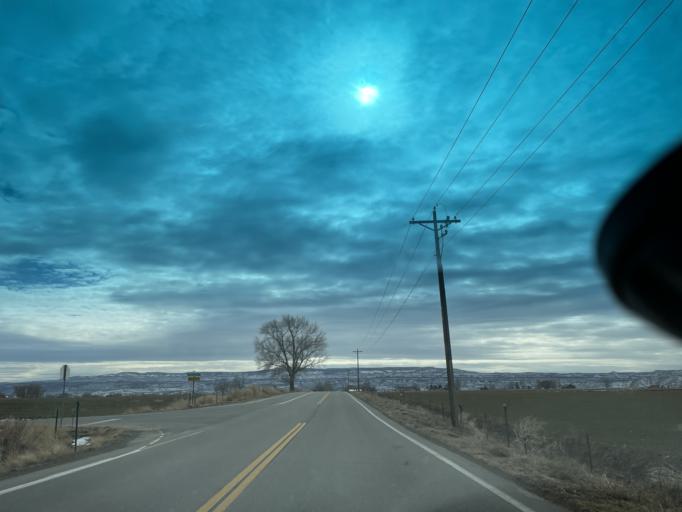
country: US
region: Colorado
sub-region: Mesa County
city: Loma
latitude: 39.2178
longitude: -108.8129
